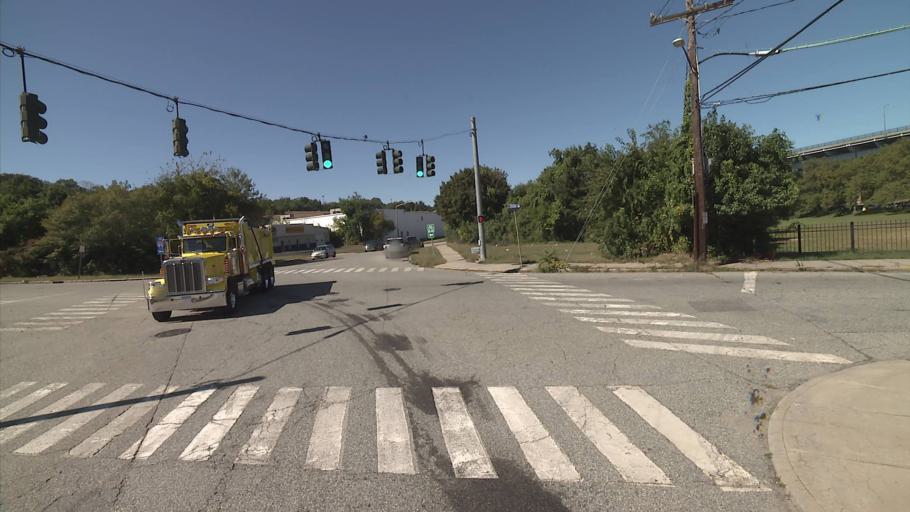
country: US
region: Connecticut
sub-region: New London County
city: New London
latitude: 41.3614
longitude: -72.0973
